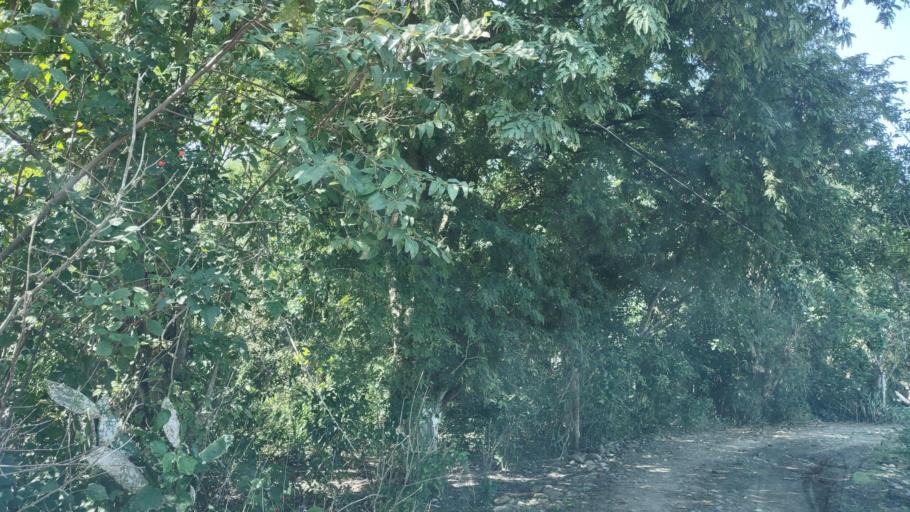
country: MX
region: Puebla
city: Espinal
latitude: 20.2509
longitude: -97.3416
